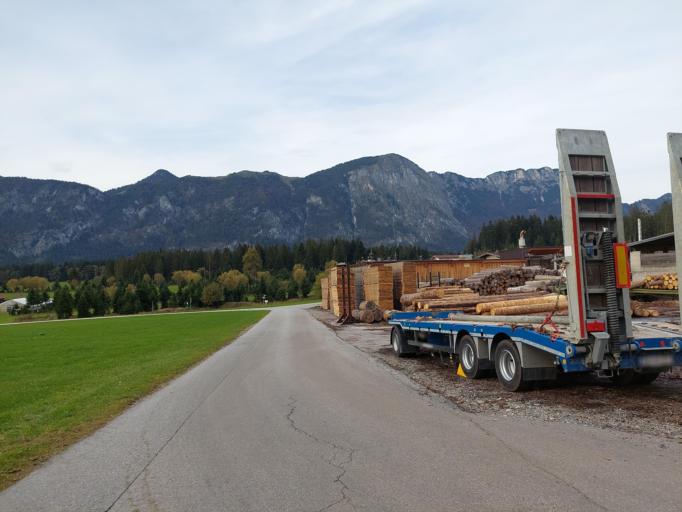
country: AT
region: Tyrol
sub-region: Politischer Bezirk Kufstein
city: Angath
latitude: 47.5012
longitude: 12.0384
